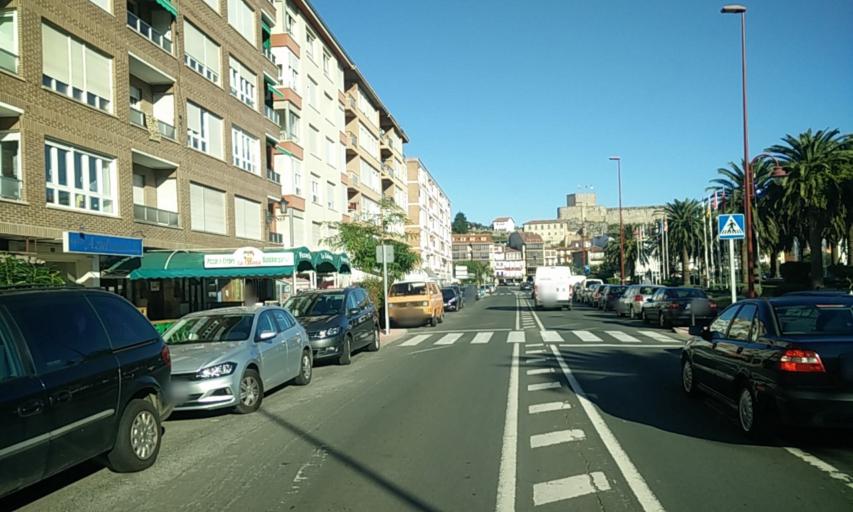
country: ES
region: Cantabria
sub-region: Provincia de Cantabria
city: San Vicente de la Barquera
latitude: 43.3827
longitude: -4.3981
